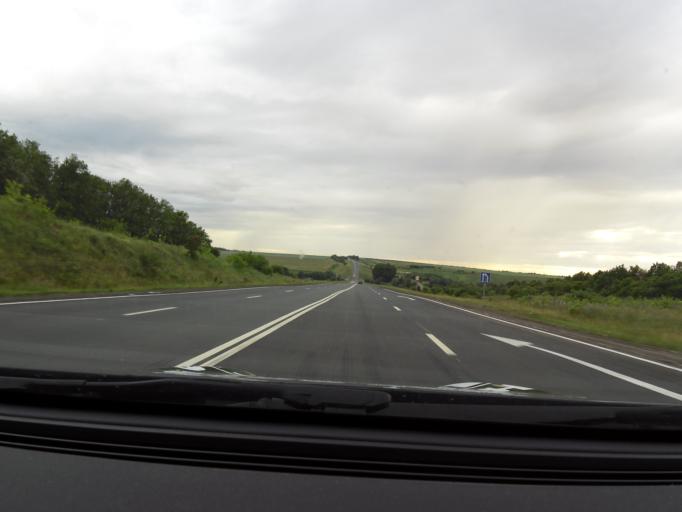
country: RU
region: Chuvashia
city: Yantikovo
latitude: 55.8089
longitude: 47.9773
